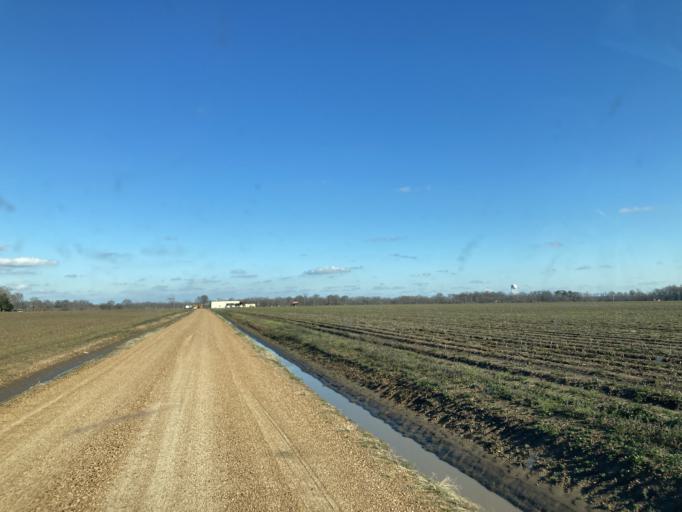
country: US
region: Mississippi
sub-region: Yazoo County
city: Yazoo City
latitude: 32.9287
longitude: -90.5055
